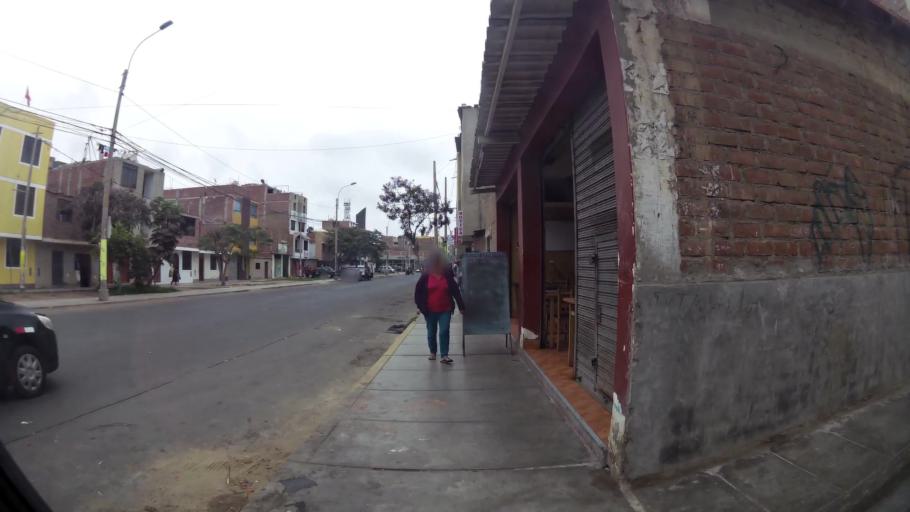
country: PE
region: La Libertad
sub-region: Provincia de Trujillo
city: Trujillo
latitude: -8.1225
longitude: -79.0331
